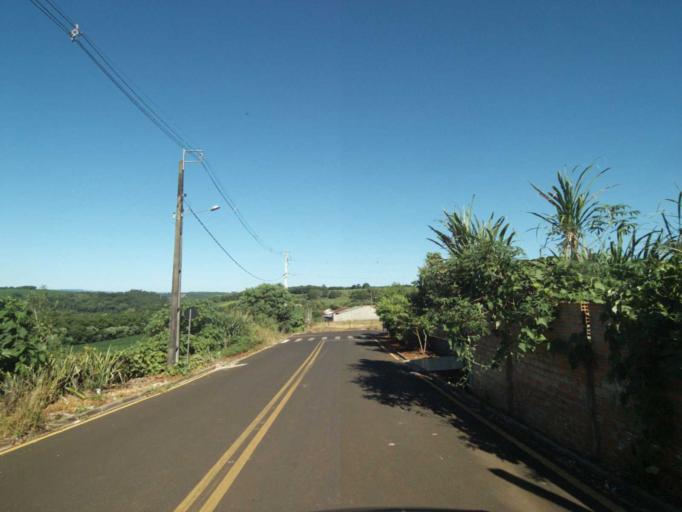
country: BR
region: Parana
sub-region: Coronel Vivida
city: Coronel Vivida
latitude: -25.9665
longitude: -52.8095
